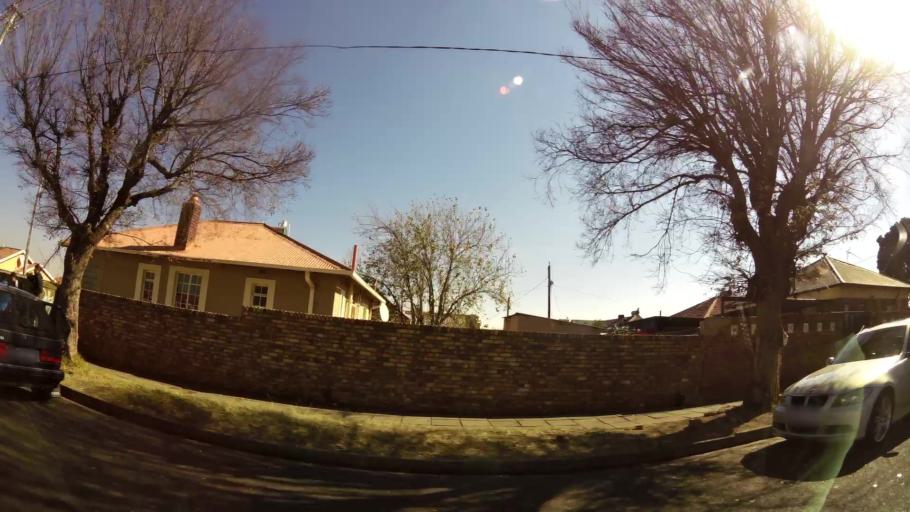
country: ZA
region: Gauteng
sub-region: City of Johannesburg Metropolitan Municipality
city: Johannesburg
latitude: -26.1904
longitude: 27.9756
